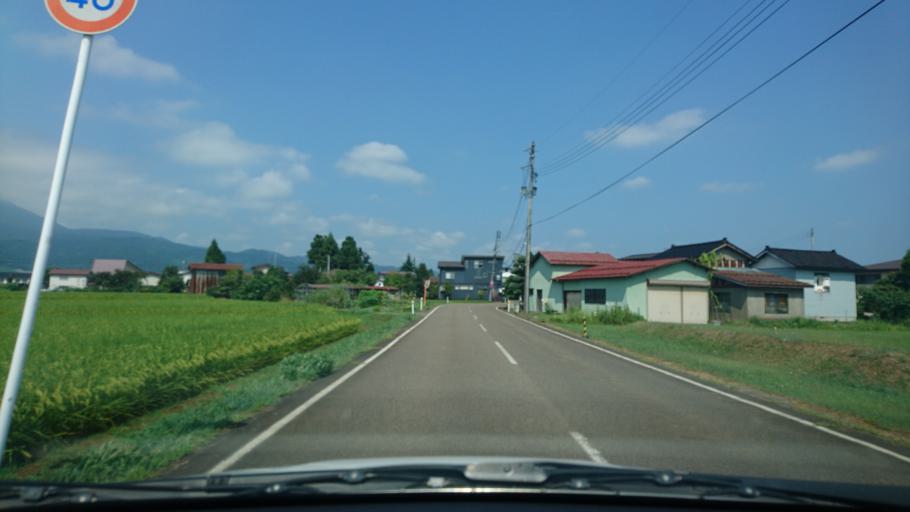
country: JP
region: Niigata
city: Arai
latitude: 37.0666
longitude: 138.2609
